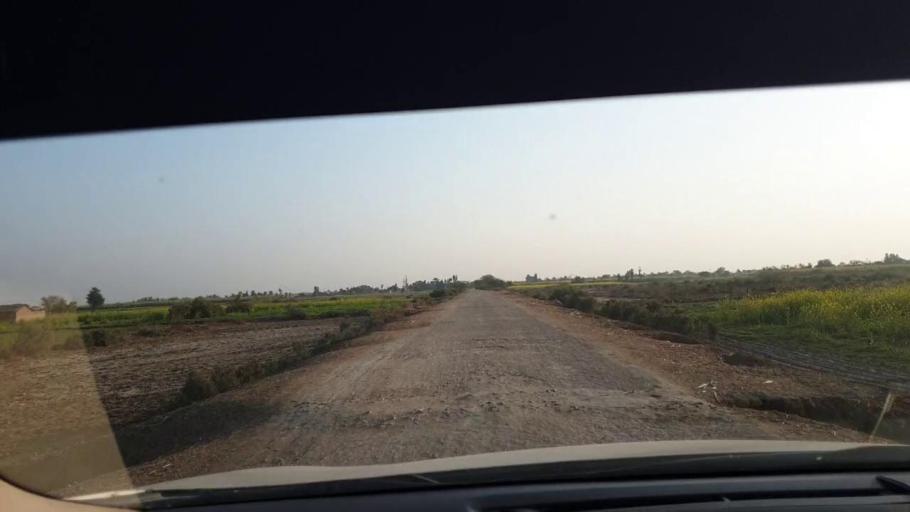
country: PK
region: Sindh
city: Berani
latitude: 25.8448
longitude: 68.8167
